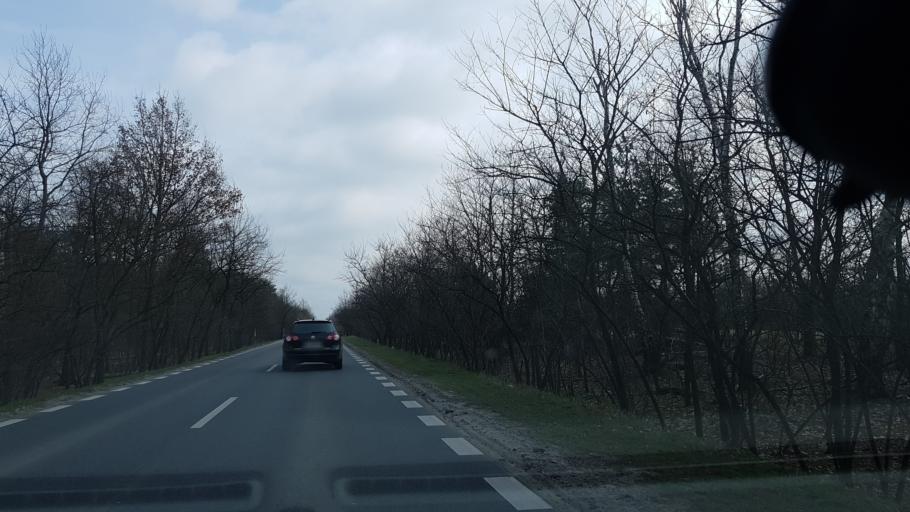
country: PL
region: Masovian Voivodeship
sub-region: Warszawa
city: Wesola
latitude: 52.2549
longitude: 21.2158
